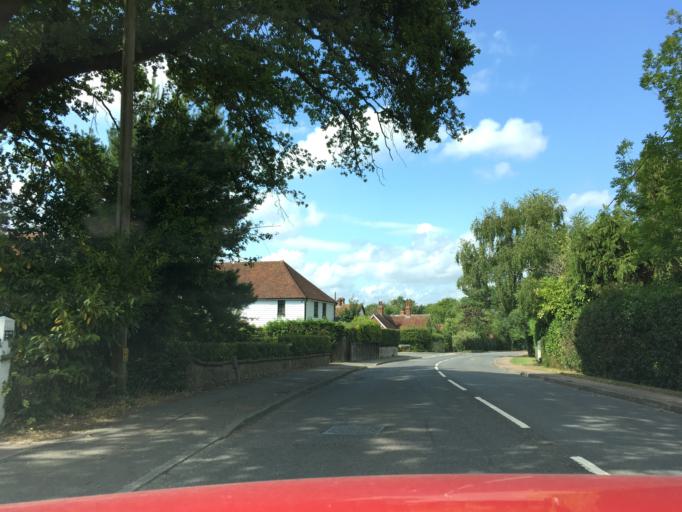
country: GB
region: England
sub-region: Kent
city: Headcorn
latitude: 51.1175
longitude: 0.6439
